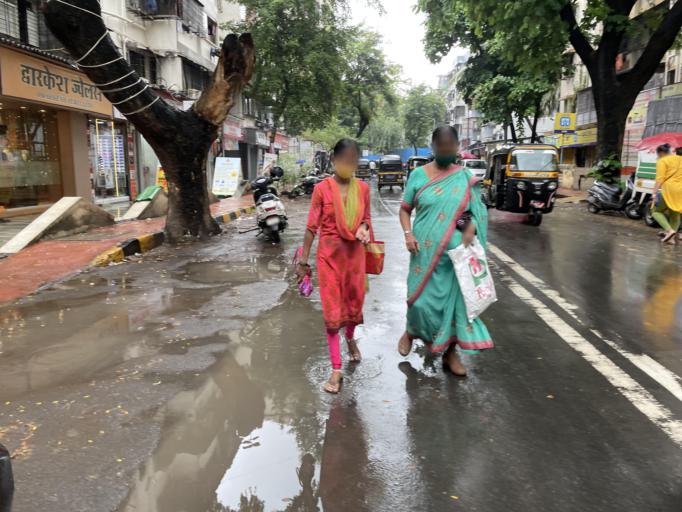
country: IN
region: Maharashtra
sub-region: Mumbai Suburban
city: Borivli
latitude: 19.2537
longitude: 72.8606
